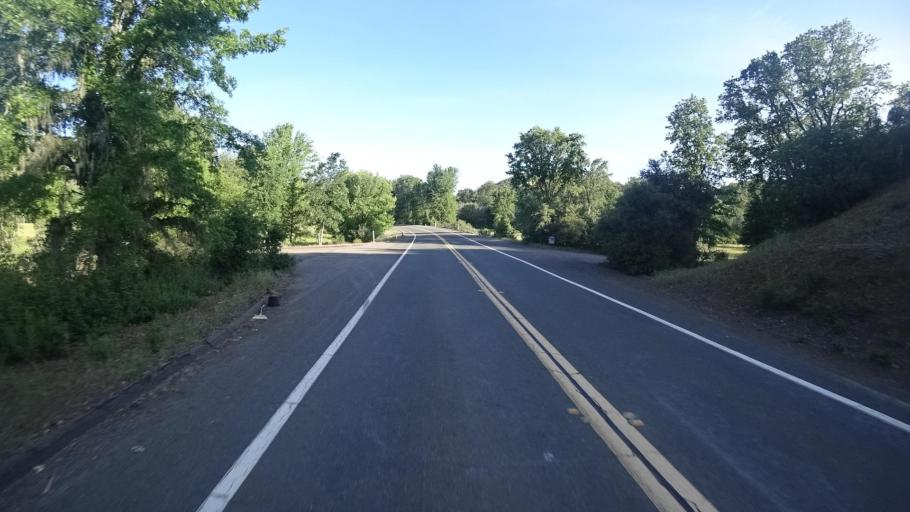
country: US
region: California
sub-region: Lake County
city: North Lakeport
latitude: 39.1049
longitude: -122.9709
